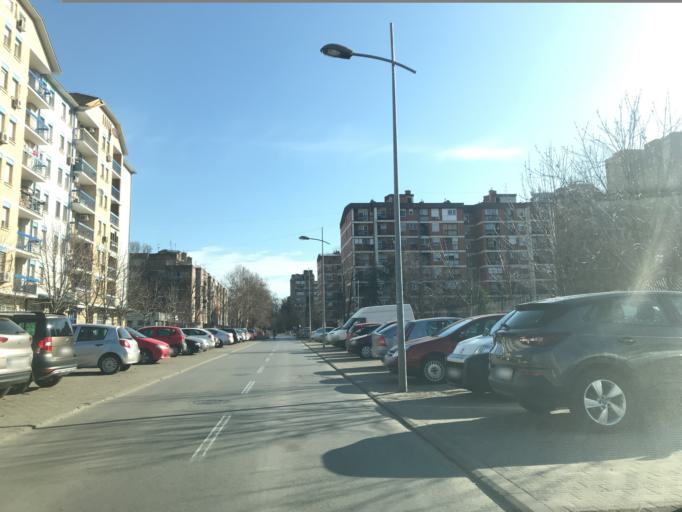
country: RS
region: Autonomna Pokrajina Vojvodina
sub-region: Juznobacki Okrug
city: Novi Sad
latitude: 45.2361
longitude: 19.8306
